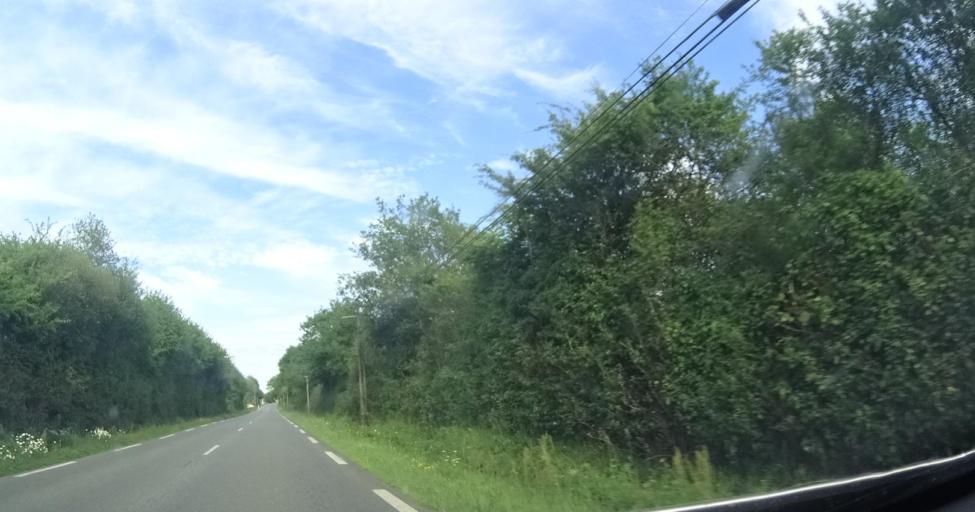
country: FR
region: Pays de la Loire
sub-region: Departement de la Loire-Atlantique
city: Heric
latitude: 47.4134
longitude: -1.6772
